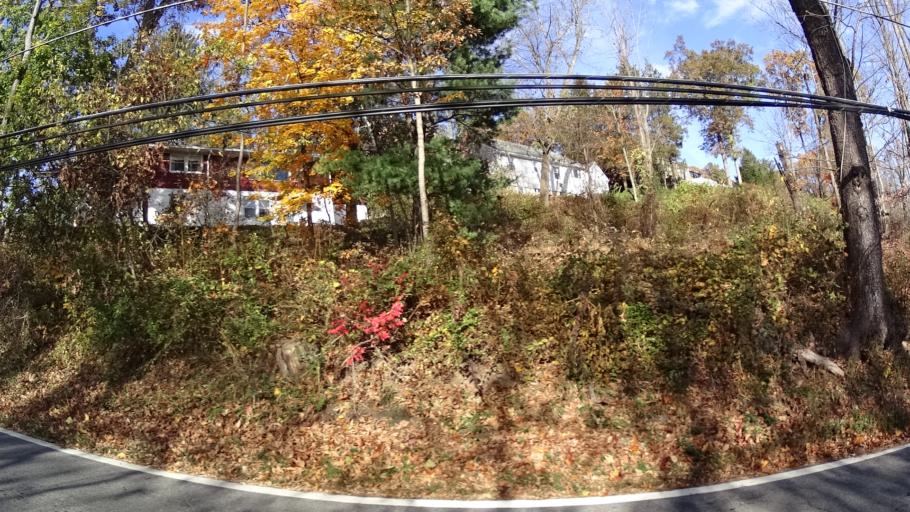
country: US
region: New Jersey
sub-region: Union County
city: Berkeley Heights
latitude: 40.6826
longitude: -74.4795
